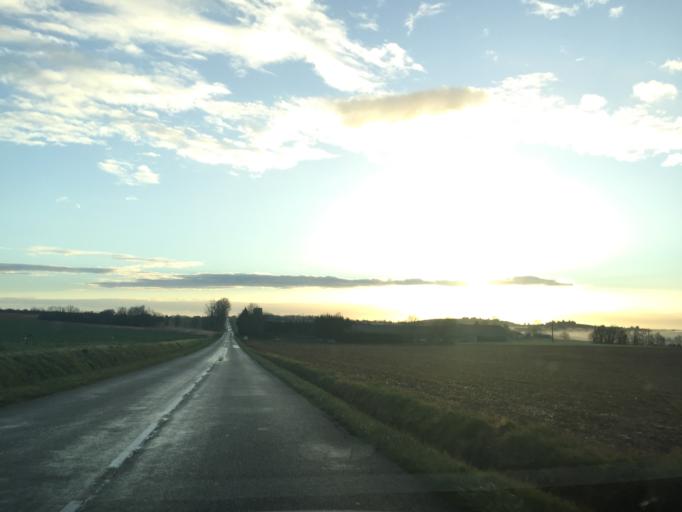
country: FR
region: Aquitaine
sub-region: Departement de la Dordogne
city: Saint-Aulaye
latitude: 45.2789
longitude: 0.1306
